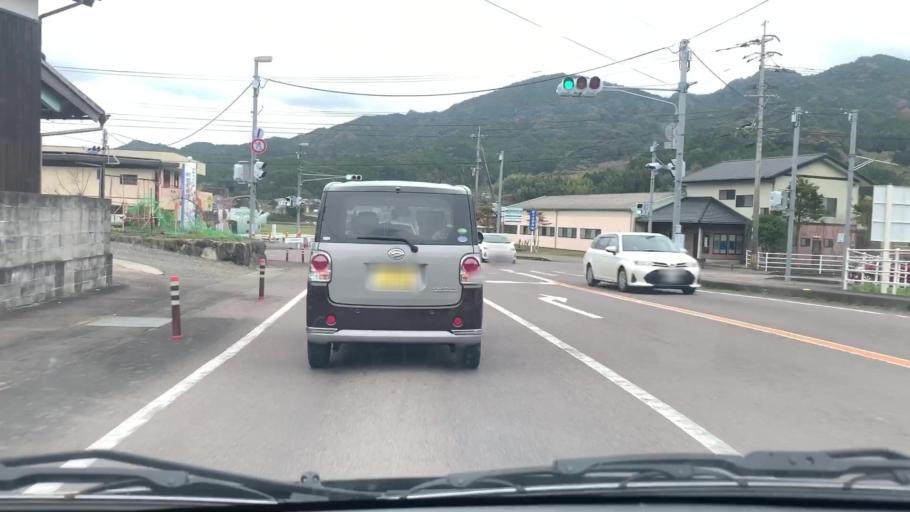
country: JP
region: Saga Prefecture
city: Ureshinomachi-shimojuku
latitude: 33.0876
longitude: 130.0200
